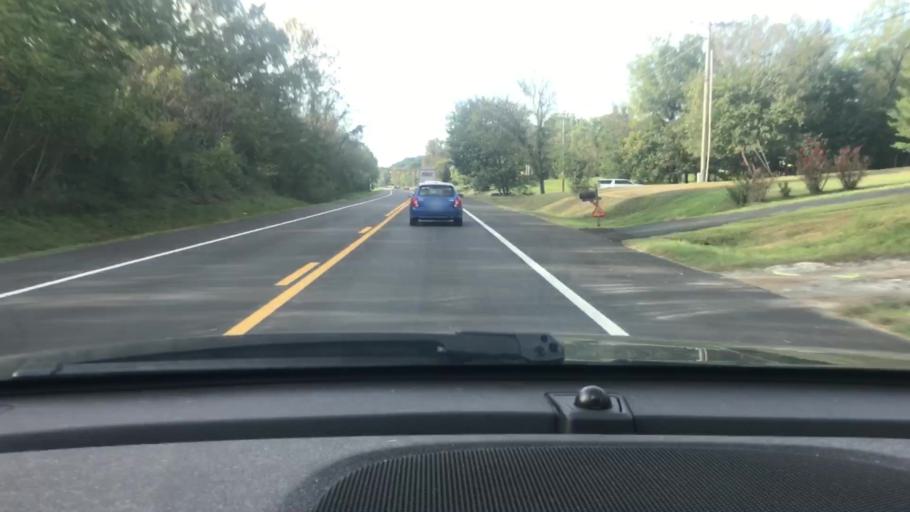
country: US
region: Tennessee
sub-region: Williamson County
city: Franklin
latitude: 35.9464
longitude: -86.9462
